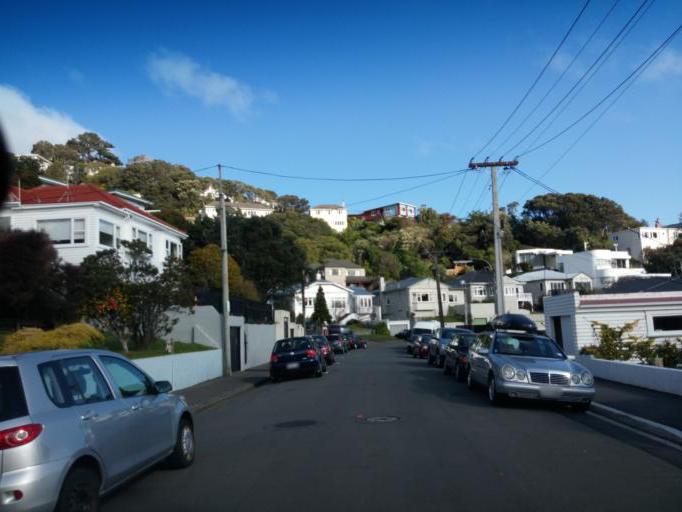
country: NZ
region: Wellington
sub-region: Wellington City
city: Wellington
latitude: -41.3247
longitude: 174.8257
